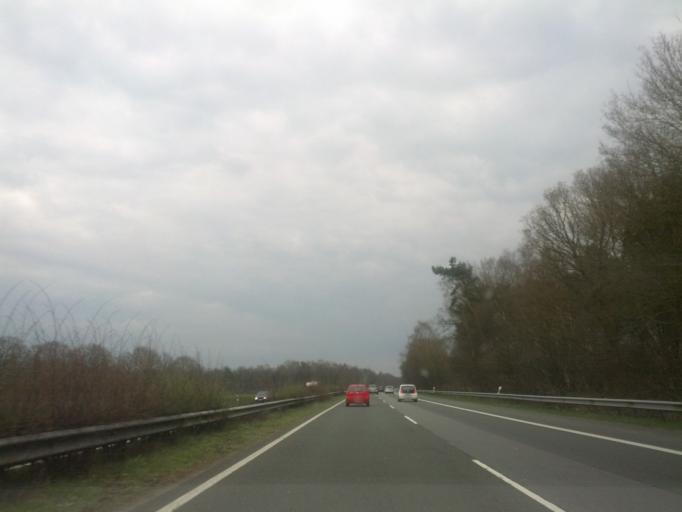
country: DE
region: Lower Saxony
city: Wiefelstede
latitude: 53.2061
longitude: 8.0785
